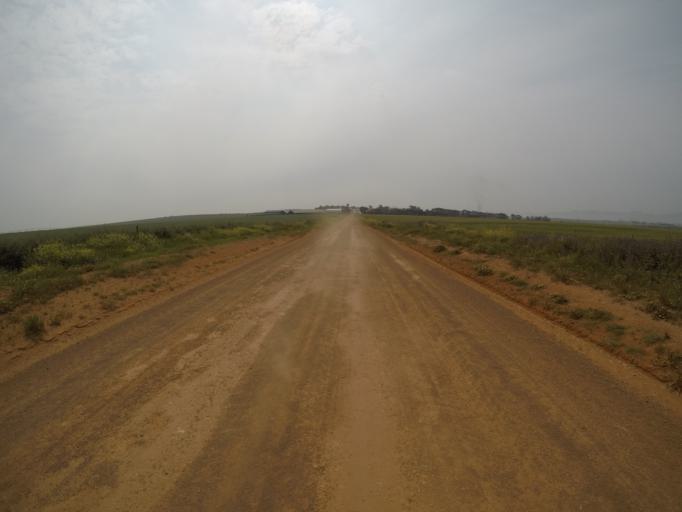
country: ZA
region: Western Cape
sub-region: City of Cape Town
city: Kraaifontein
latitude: -33.7101
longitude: 18.6879
